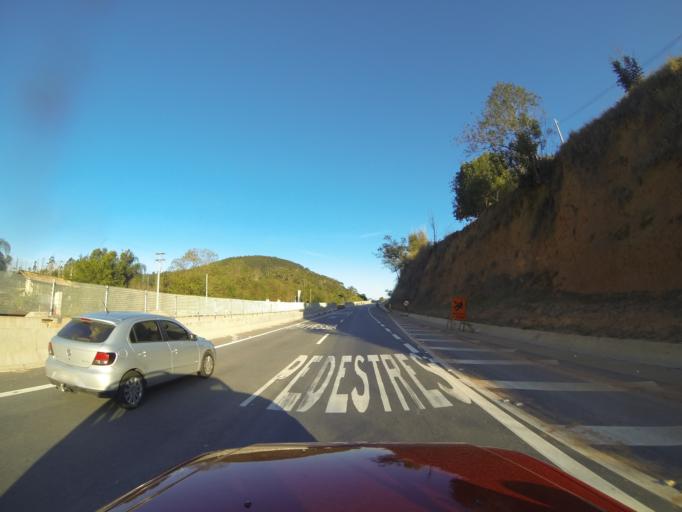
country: BR
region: Sao Paulo
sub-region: Santa Branca
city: Santa Branca
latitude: -23.3527
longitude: -45.7058
